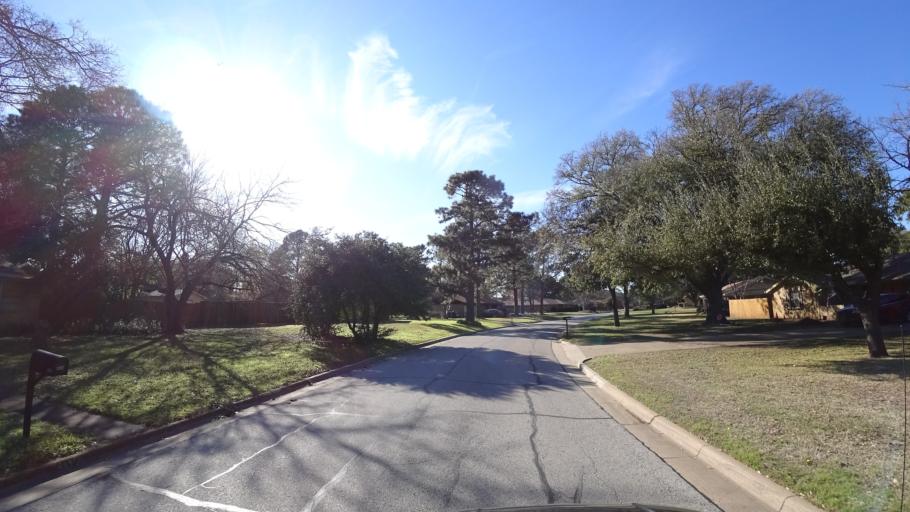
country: US
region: Texas
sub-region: Denton County
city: Lewisville
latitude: 33.0735
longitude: -97.0148
